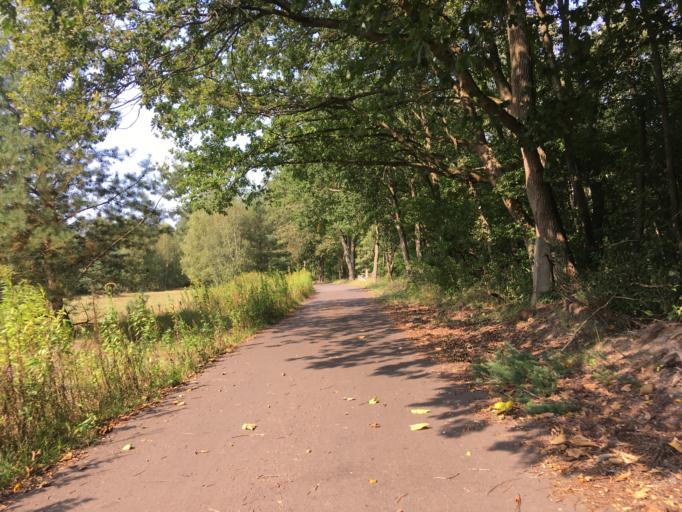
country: DE
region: Berlin
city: Falkenhagener Feld
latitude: 52.5957
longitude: 13.1731
